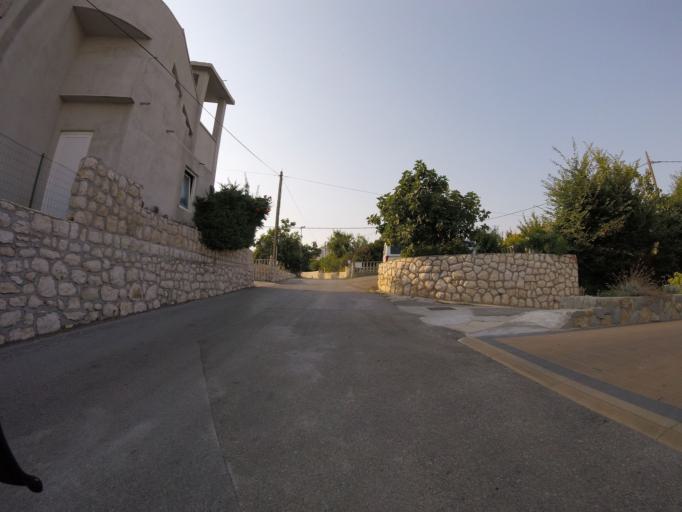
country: HR
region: Primorsko-Goranska
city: Lopar
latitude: 44.8321
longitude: 14.7300
